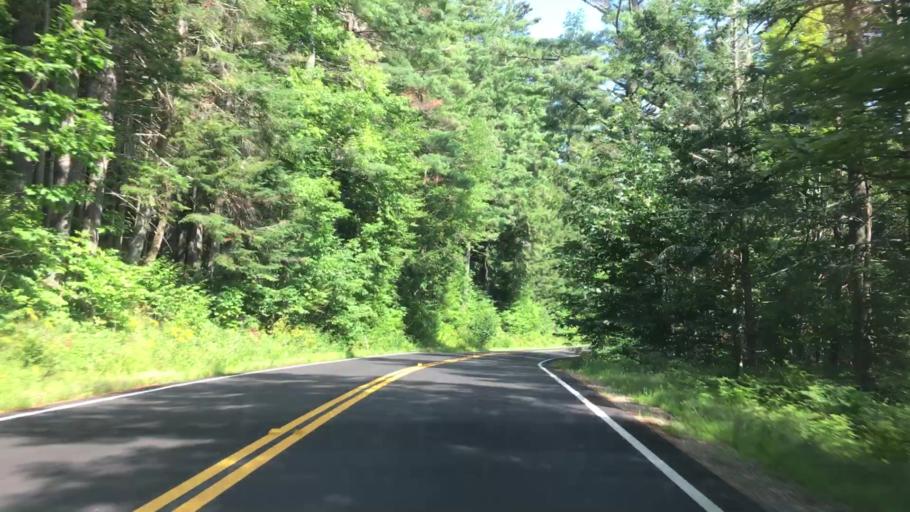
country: US
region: New Hampshire
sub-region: Grafton County
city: North Haverhill
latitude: 44.1018
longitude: -71.8559
